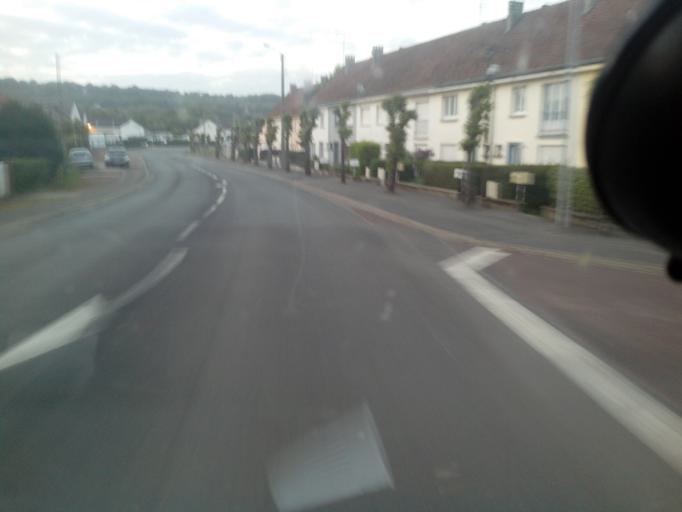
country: FR
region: Nord-Pas-de-Calais
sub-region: Departement du Pas-de-Calais
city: Hesdin
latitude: 50.3746
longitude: 2.0306
